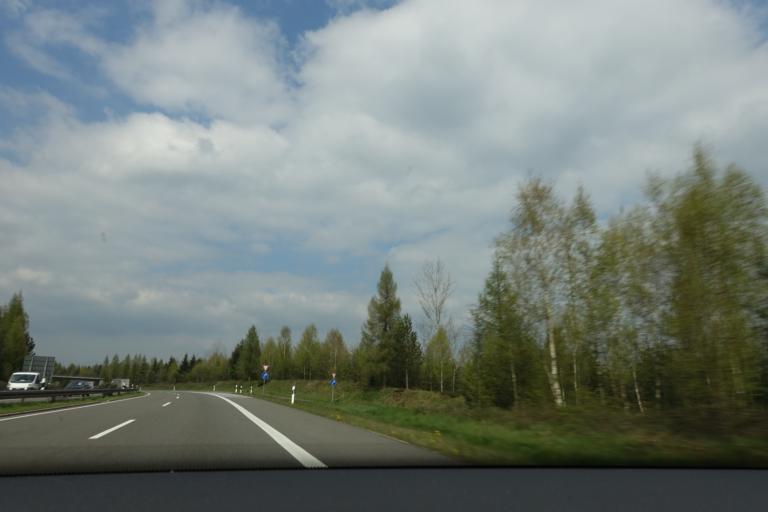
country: DE
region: Saxony
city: Gornau
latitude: 50.7637
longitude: 13.0161
